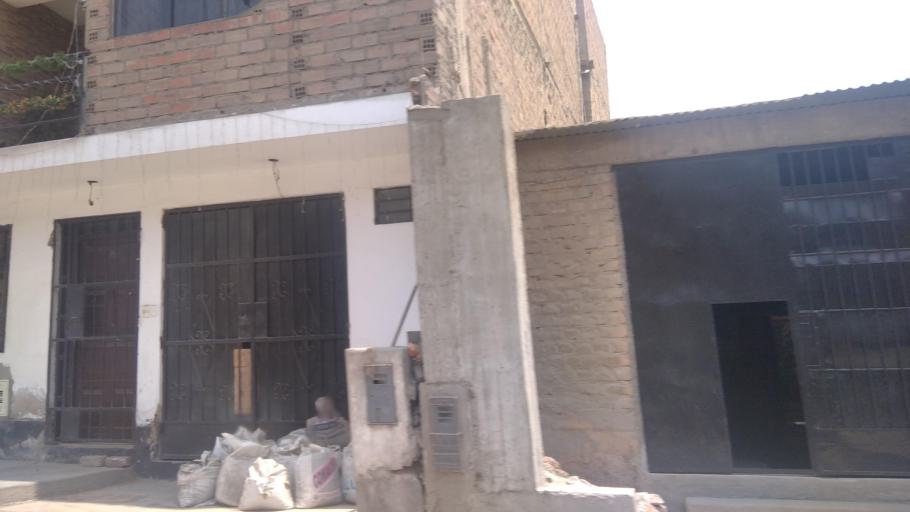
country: PE
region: Lima
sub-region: Lima
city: Independencia
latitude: -11.9634
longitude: -76.9820
